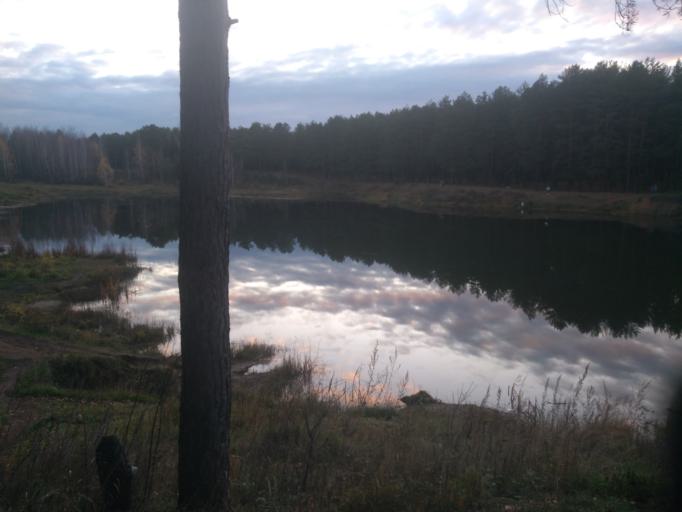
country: RU
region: Tatarstan
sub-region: Tukayevskiy Rayon
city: Naberezhnyye Chelny
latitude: 55.7596
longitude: 52.3924
